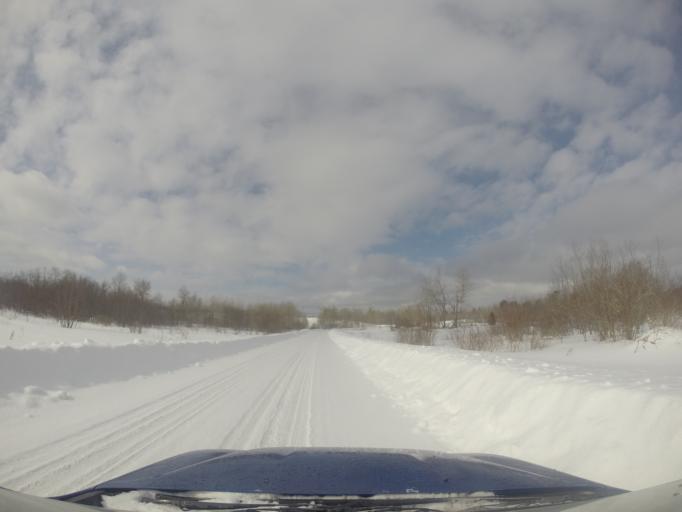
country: CA
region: Ontario
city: Greater Sudbury
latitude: 46.1047
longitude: -80.6704
